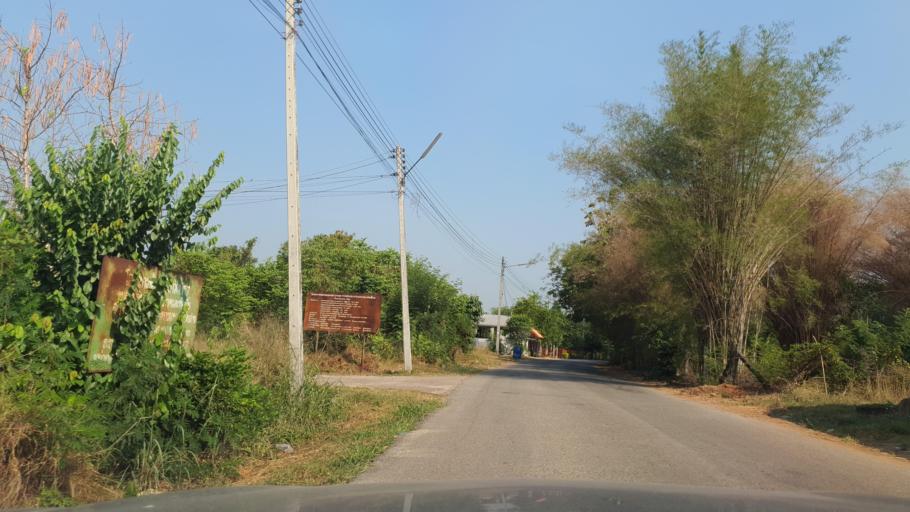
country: TH
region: Kanchanaburi
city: Kanchanaburi
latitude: 14.0689
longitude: 99.4854
